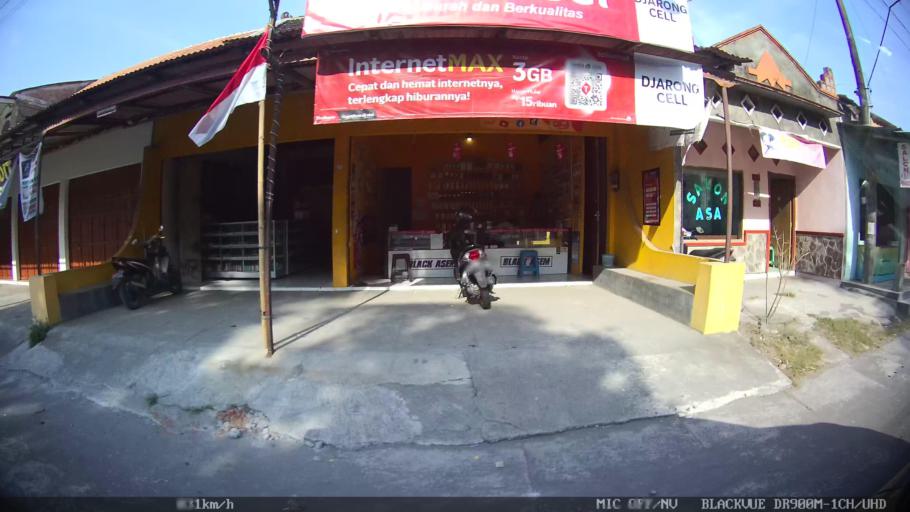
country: ID
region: Daerah Istimewa Yogyakarta
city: Pandak
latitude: -7.8966
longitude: 110.2983
